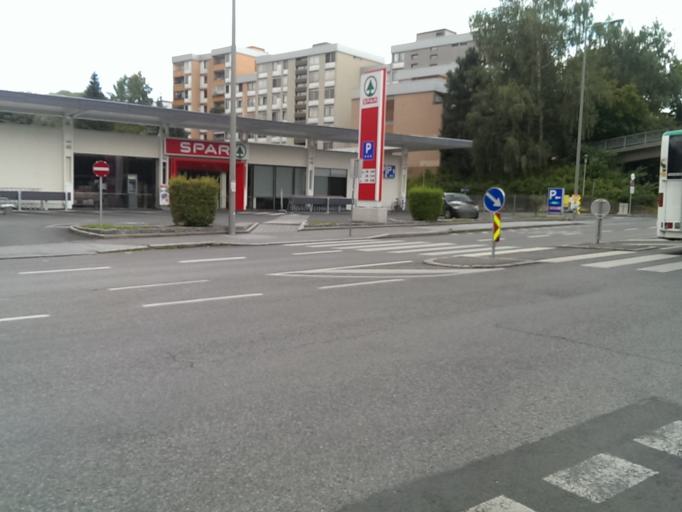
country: AT
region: Styria
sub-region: Graz Stadt
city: Graz
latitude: 47.0617
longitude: 15.4670
